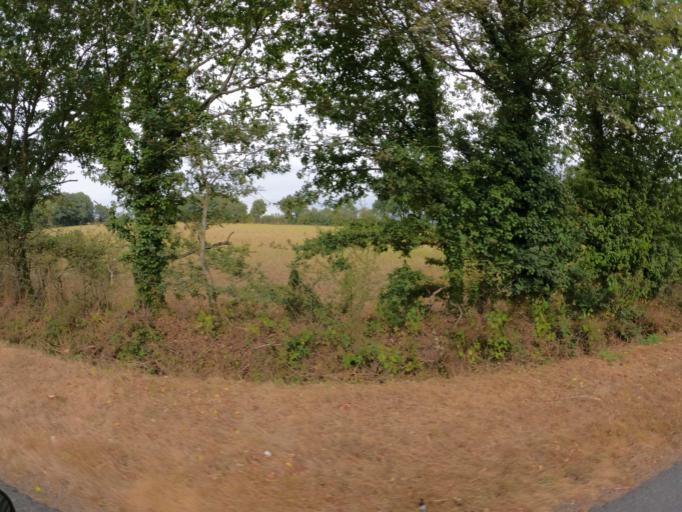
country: FR
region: Pays de la Loire
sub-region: Departement de Maine-et-Loire
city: Le Longeron
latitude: 47.0371
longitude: -1.0383
